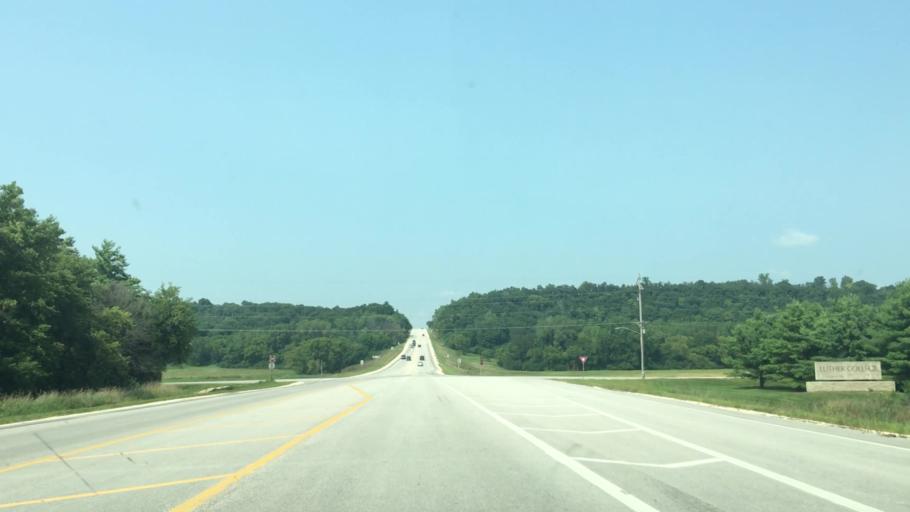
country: US
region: Iowa
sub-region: Winneshiek County
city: Decorah
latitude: 43.3192
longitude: -91.8140
